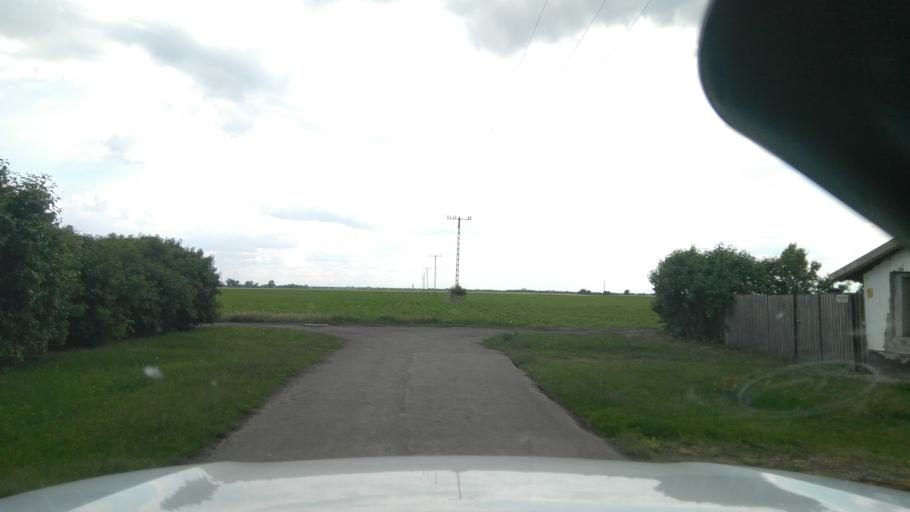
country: HU
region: Bekes
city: Magyarbanhegyes
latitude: 46.4481
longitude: 20.9715
